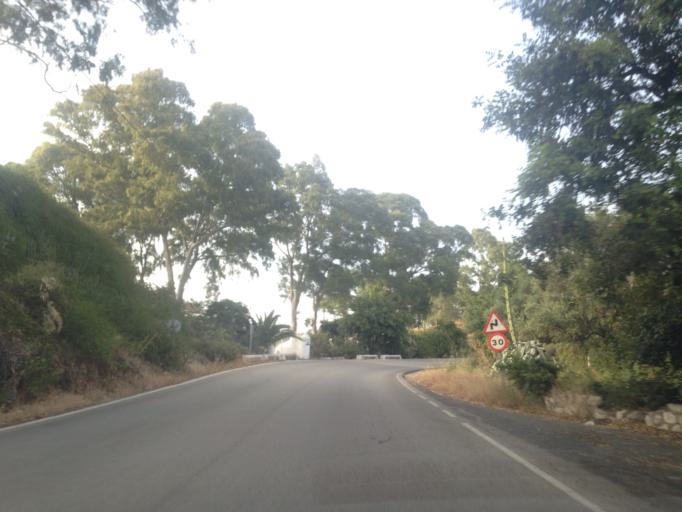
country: ES
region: Andalusia
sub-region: Provincia de Malaga
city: Malaga
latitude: 36.7451
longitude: -4.4109
